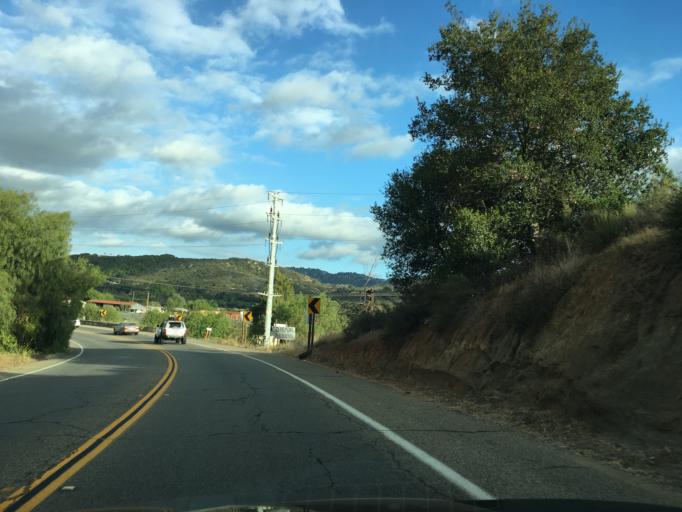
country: US
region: California
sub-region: San Diego County
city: Valley Center
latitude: 33.2289
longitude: -117.0184
